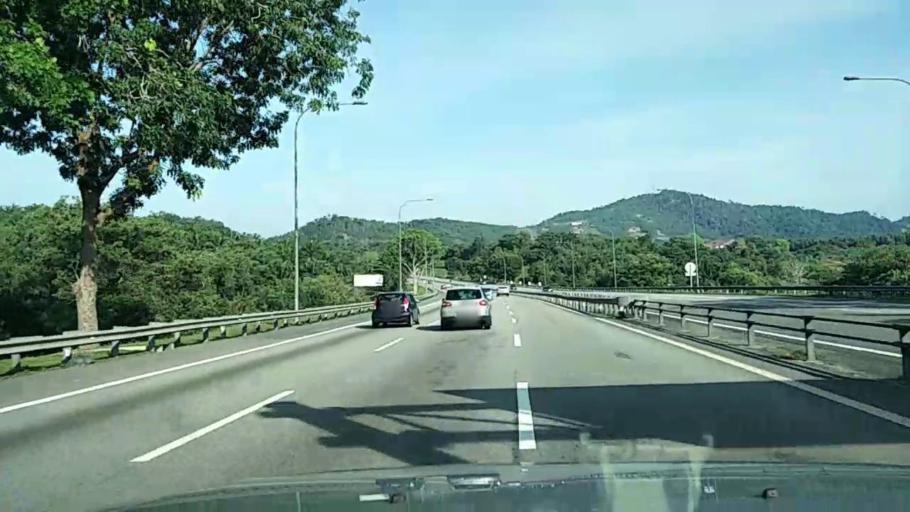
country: MY
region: Negeri Sembilan
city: Kampung Baharu Nilai
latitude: 2.8557
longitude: 101.7710
